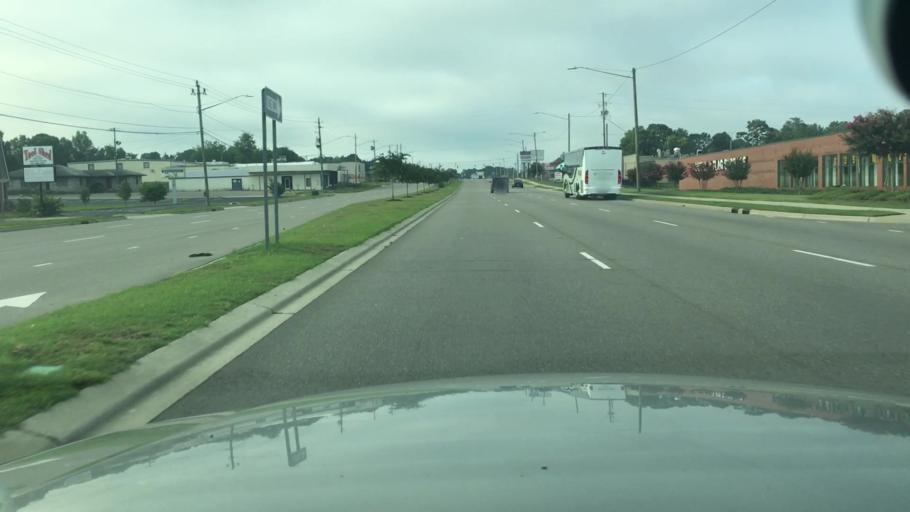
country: US
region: North Carolina
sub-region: Cumberland County
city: Fort Bragg
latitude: 35.0961
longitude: -78.9562
